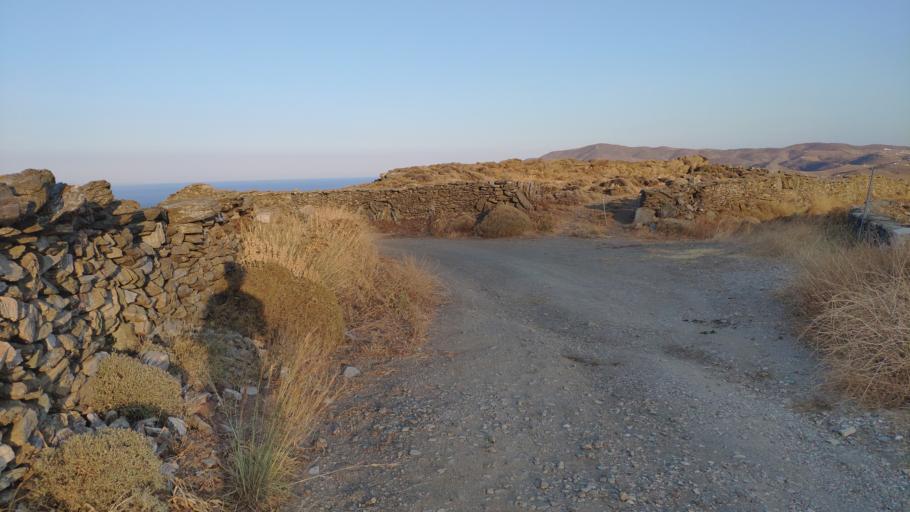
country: GR
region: South Aegean
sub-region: Nomos Kykladon
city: Kythnos
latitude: 37.4570
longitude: 24.4177
